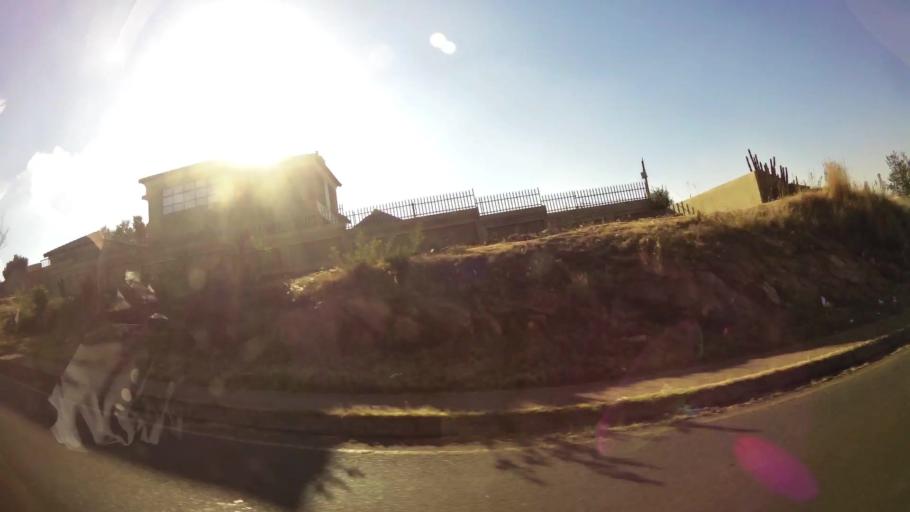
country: ZA
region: Gauteng
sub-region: City of Johannesburg Metropolitan Municipality
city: Roodepoort
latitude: -26.1515
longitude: 27.8403
